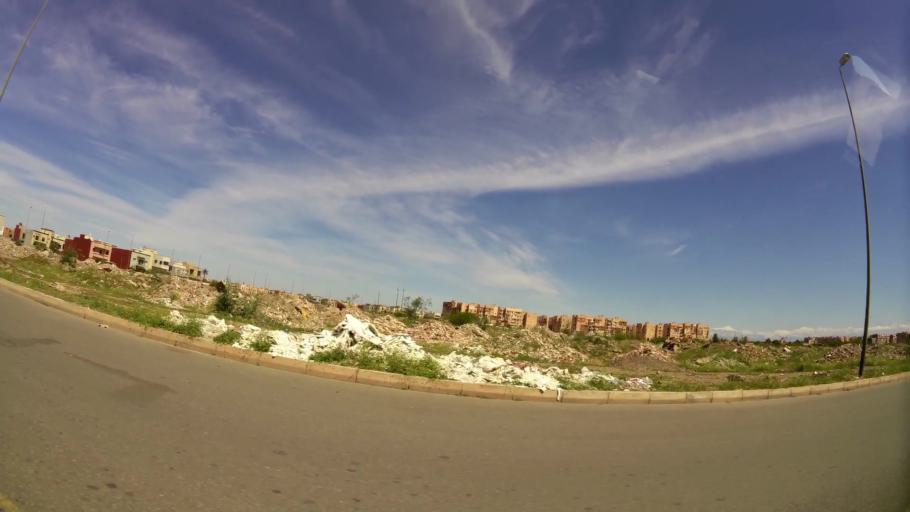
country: MA
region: Marrakech-Tensift-Al Haouz
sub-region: Marrakech
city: Marrakesh
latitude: 31.6489
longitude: -8.0791
